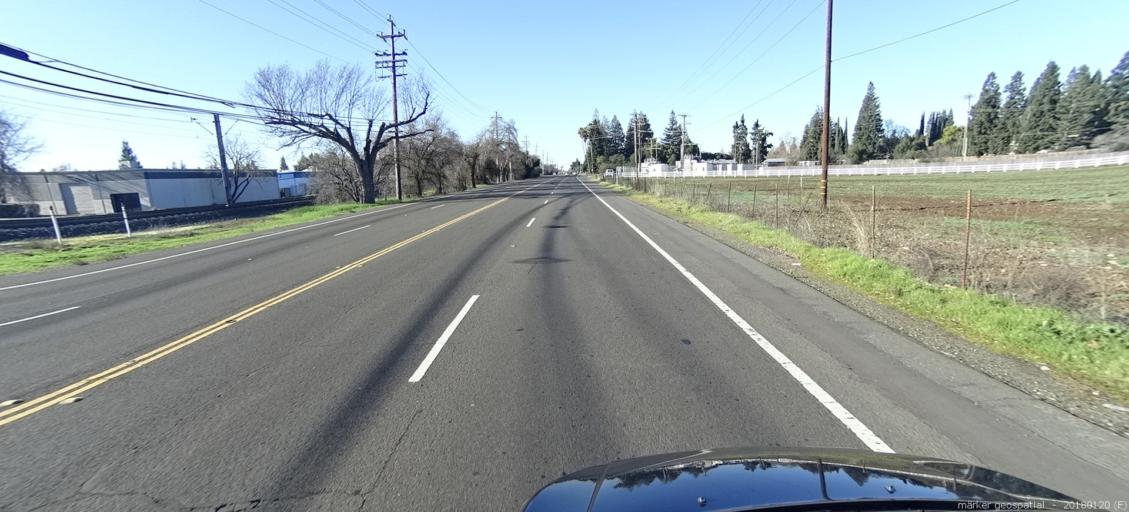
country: US
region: California
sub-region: Sacramento County
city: Rancho Cordova
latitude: 38.5779
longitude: -121.3256
